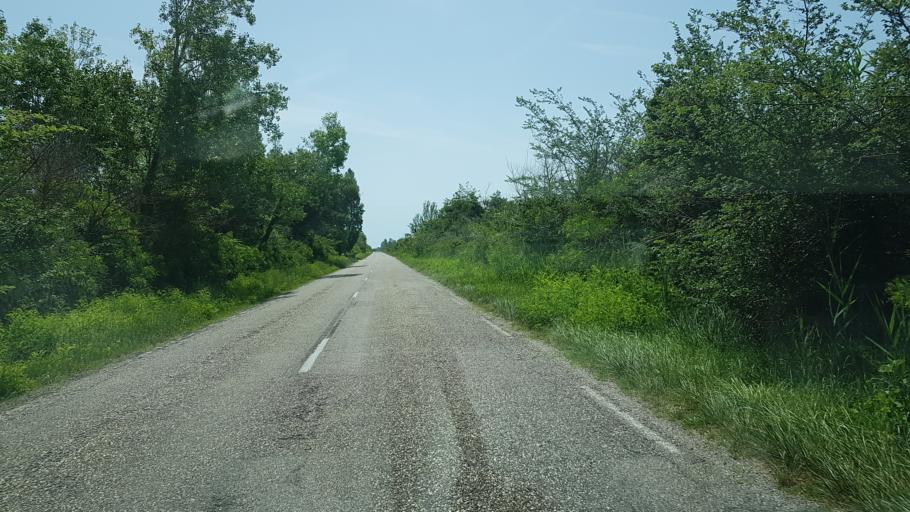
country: FR
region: Languedoc-Roussillon
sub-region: Departement du Gard
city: Saint-Gilles
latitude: 43.5866
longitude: 4.4982
